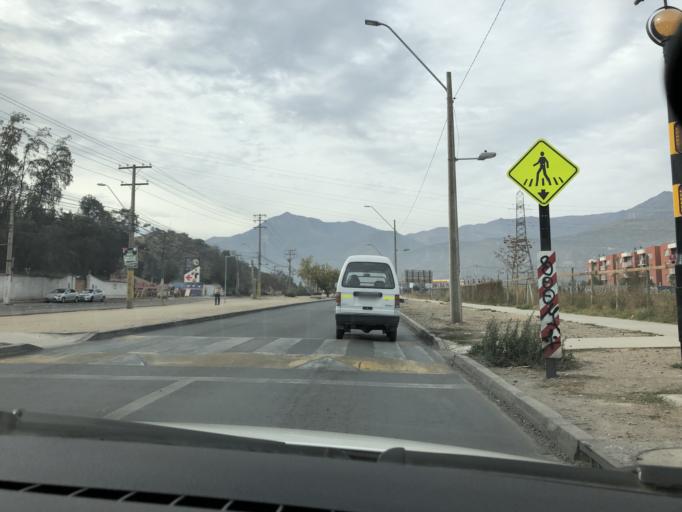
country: CL
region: Santiago Metropolitan
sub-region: Provincia de Cordillera
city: Puente Alto
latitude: -33.6106
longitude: -70.5477
